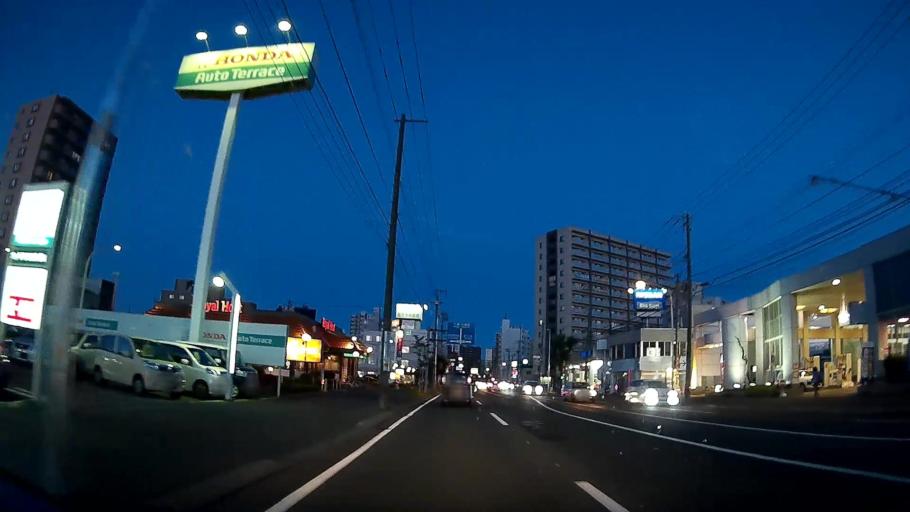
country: JP
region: Hokkaido
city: Sapporo
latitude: 43.0656
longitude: 141.3131
